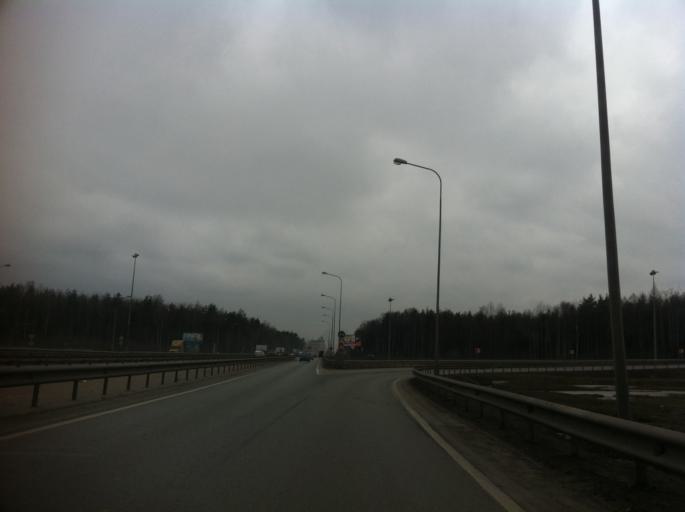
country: RU
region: St.-Petersburg
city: Krasnogvargeisky
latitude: 59.9463
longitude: 30.5405
